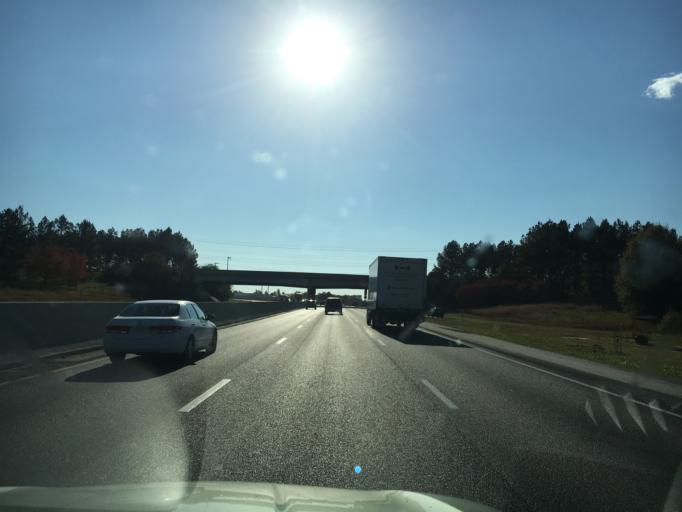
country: US
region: South Carolina
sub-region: Spartanburg County
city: Duncan
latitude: 34.8938
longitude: -82.1583
